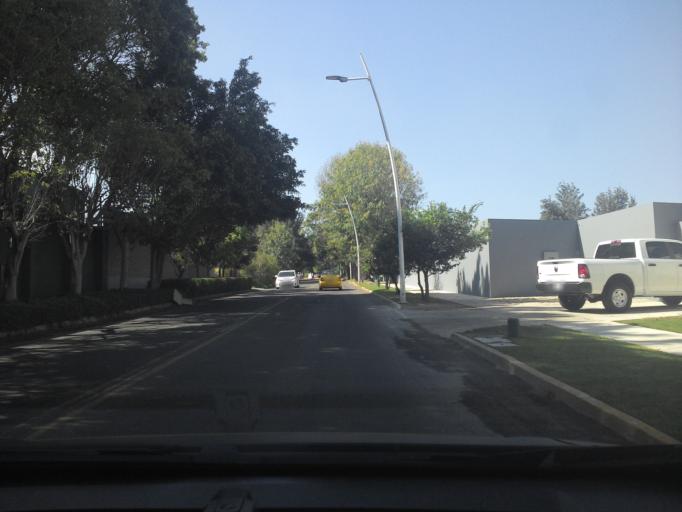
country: MX
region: Jalisco
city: Zapopan2
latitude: 20.6944
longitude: -103.4020
